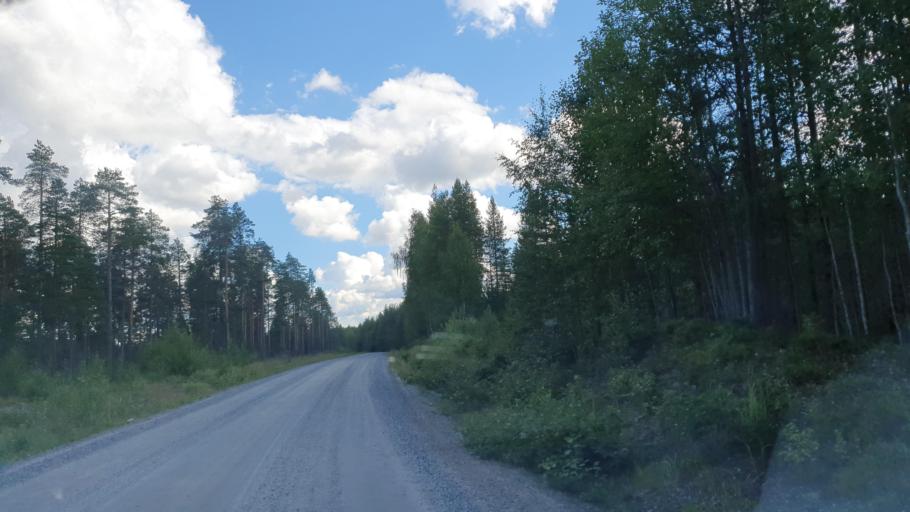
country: FI
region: Kainuu
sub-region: Kehys-Kainuu
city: Kuhmo
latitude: 64.0972
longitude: 29.4117
